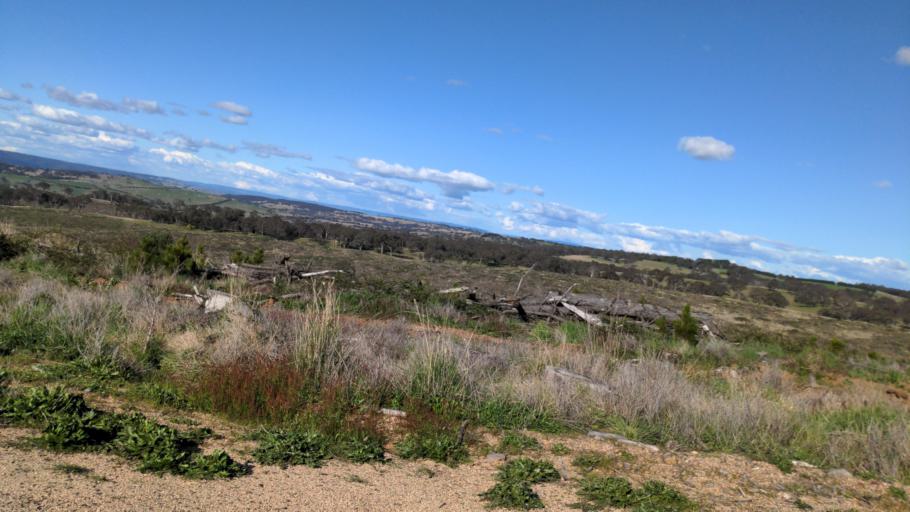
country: AU
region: New South Wales
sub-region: Blayney
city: Blayney
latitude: -33.4243
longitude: 149.3141
